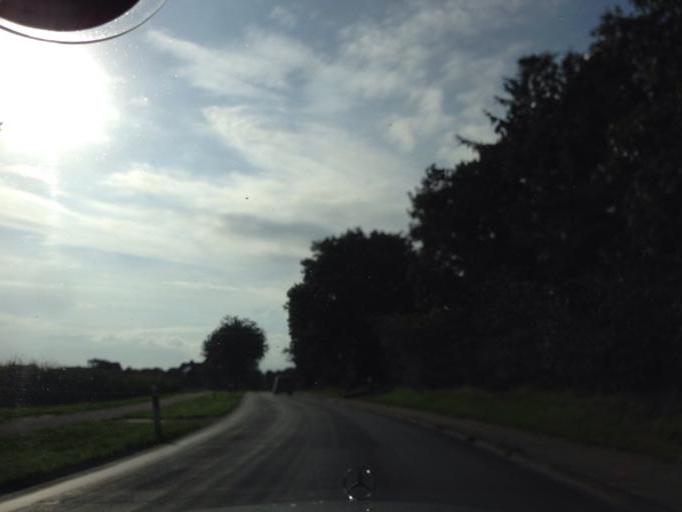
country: DE
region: Schleswig-Holstein
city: Wrixum
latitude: 54.6948
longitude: 8.5513
